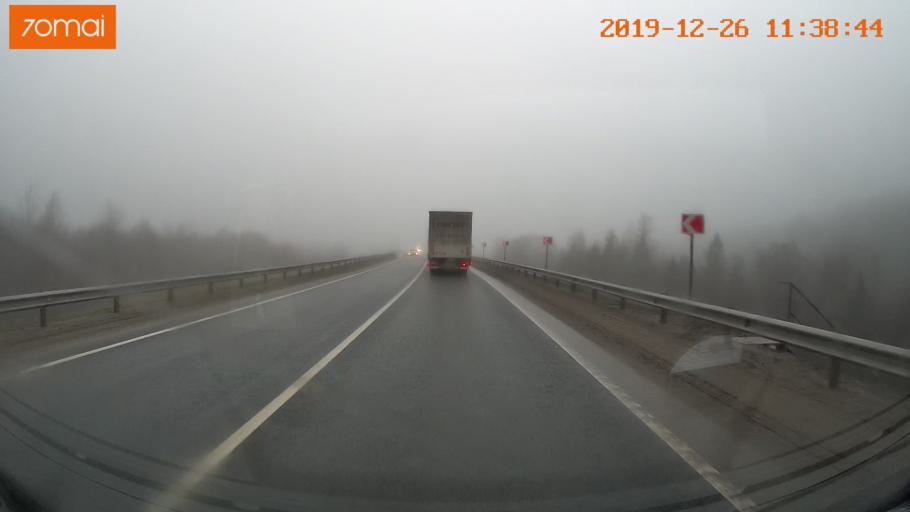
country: RU
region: Vologda
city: Sheksna
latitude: 59.2110
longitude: 38.6136
